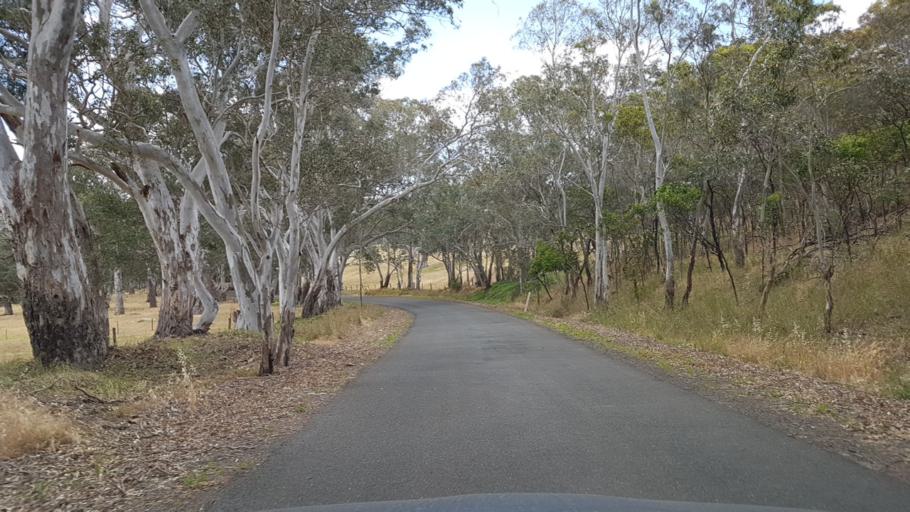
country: AU
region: South Australia
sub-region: Victor Harbor
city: Victor Harbor
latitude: -35.4789
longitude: 138.6079
